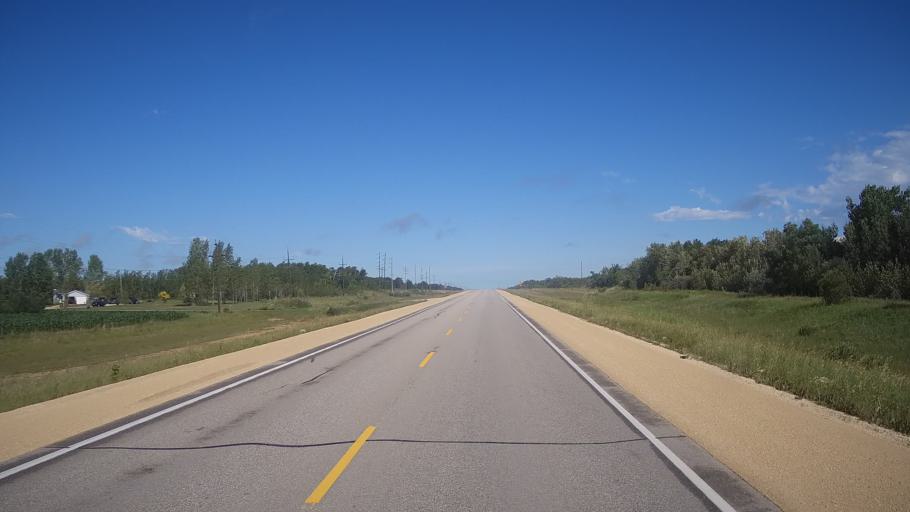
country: CA
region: Manitoba
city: Stonewall
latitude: 50.2149
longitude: -97.6742
